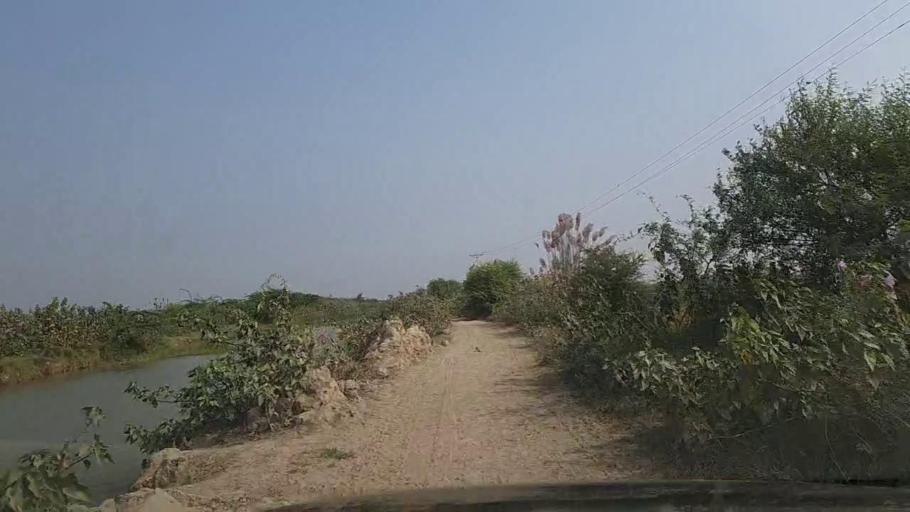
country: PK
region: Sindh
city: Thatta
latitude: 24.7579
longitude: 67.8007
